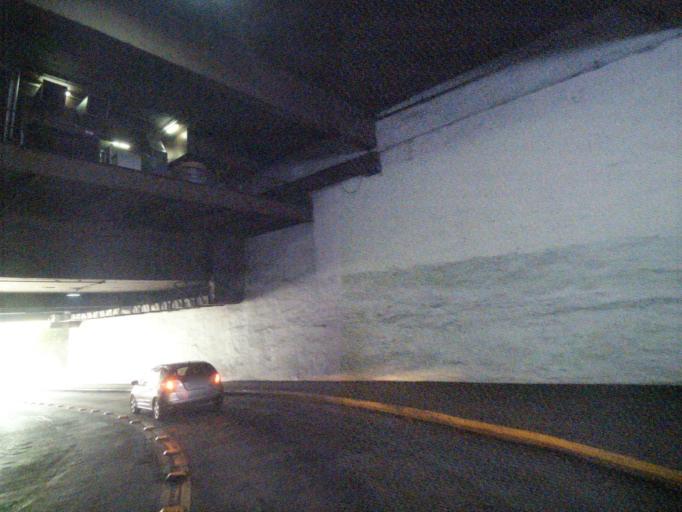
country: BR
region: Rio de Janeiro
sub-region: Rio De Janeiro
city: Rio de Janeiro
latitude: -22.9572
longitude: -43.1756
